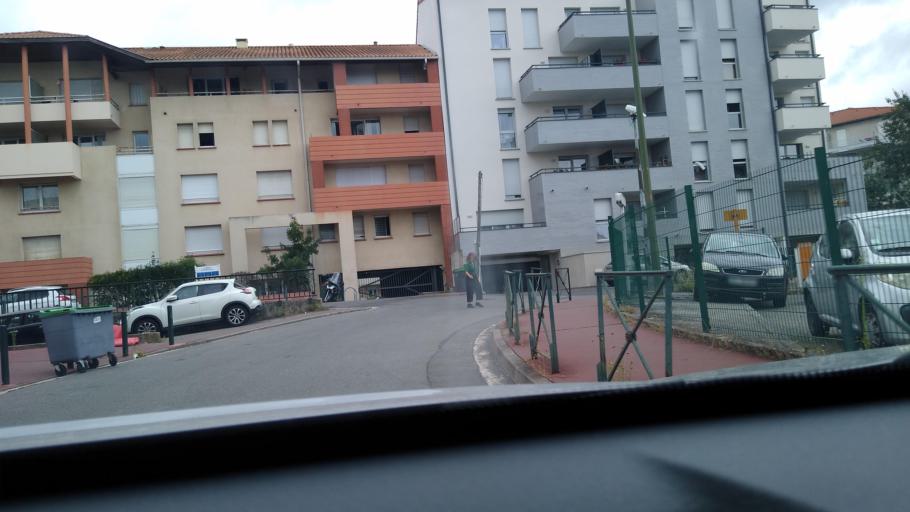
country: FR
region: Midi-Pyrenees
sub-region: Departement de la Haute-Garonne
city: Toulouse
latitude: 43.6148
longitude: 1.4620
